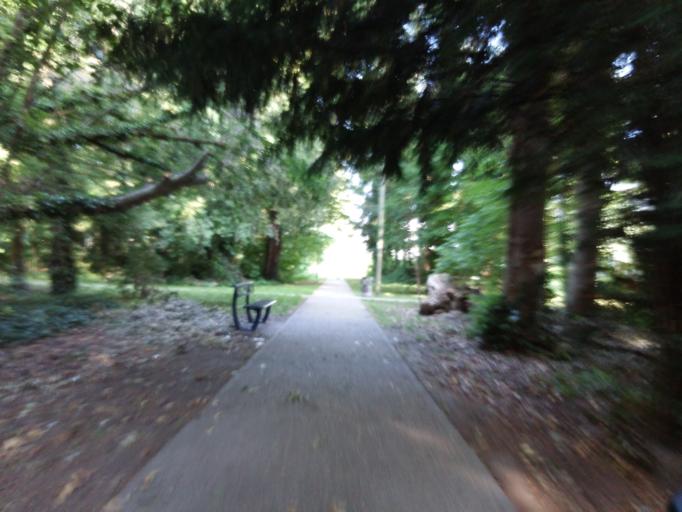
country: FR
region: Picardie
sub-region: Departement de la Somme
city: Amiens
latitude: 49.9015
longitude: 2.2903
